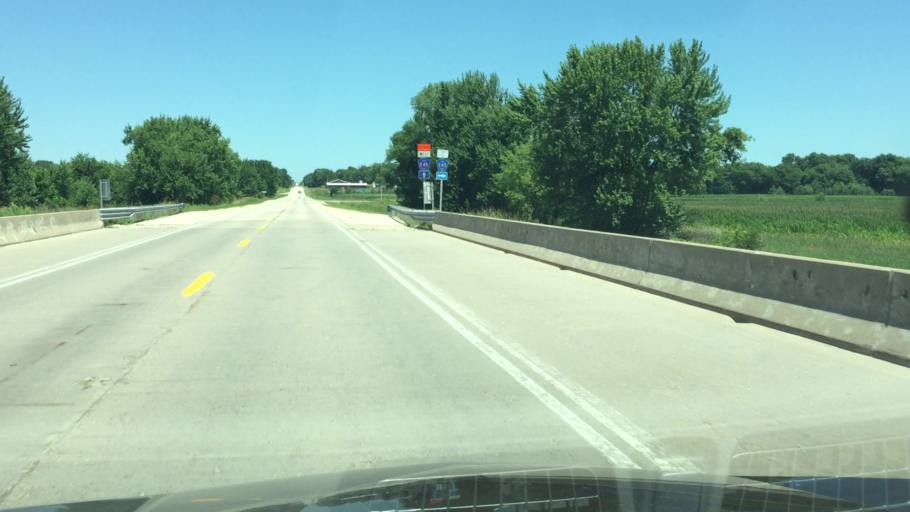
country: US
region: Iowa
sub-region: Cedar County
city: Mechanicsville
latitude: 42.0176
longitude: -91.1367
